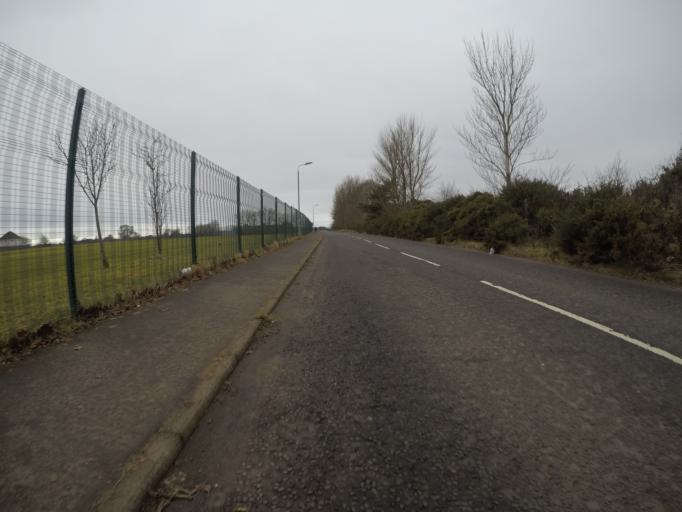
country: GB
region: Scotland
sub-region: North Ayrshire
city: Irvine
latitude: 55.6285
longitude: -4.6776
